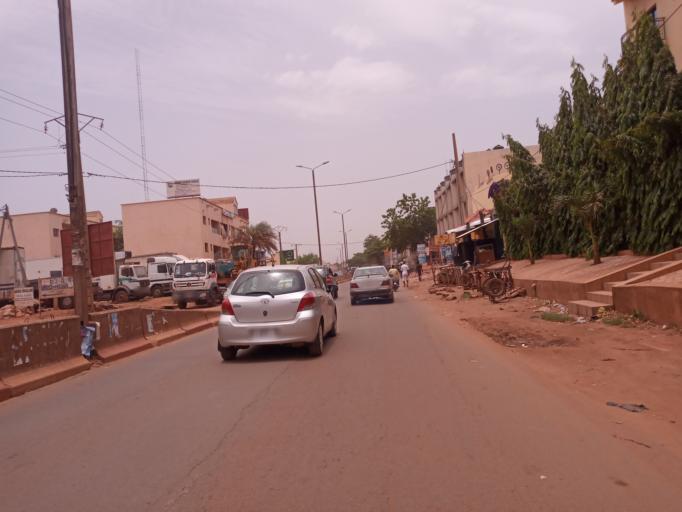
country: ML
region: Bamako
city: Bamako
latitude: 12.5882
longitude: -8.0217
